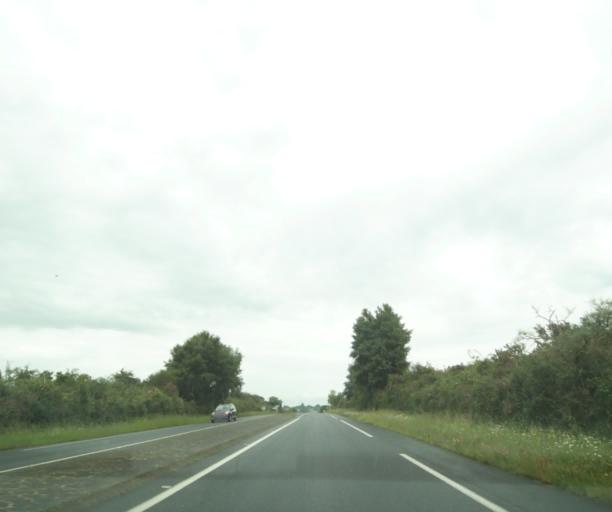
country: FR
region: Poitou-Charentes
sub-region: Departement des Deux-Sevres
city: Viennay
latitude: 46.7610
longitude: -0.2213
